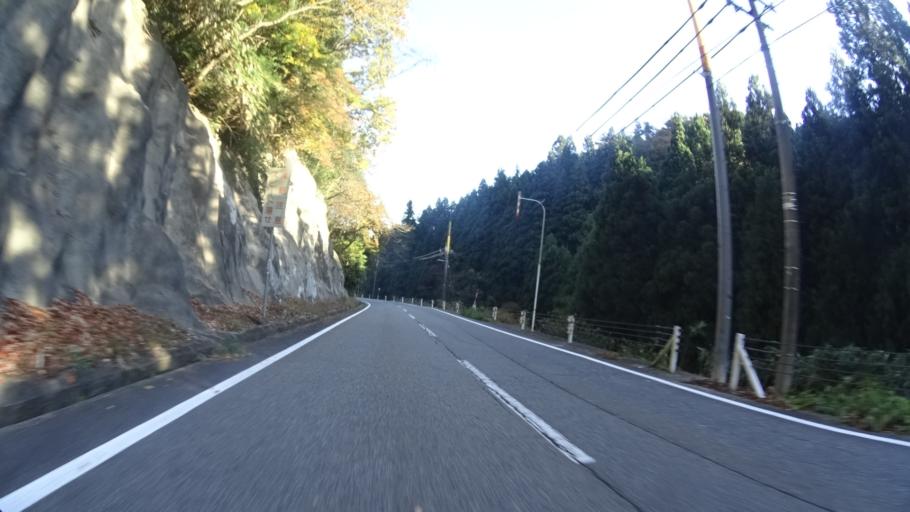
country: JP
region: Fukui
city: Maruoka
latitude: 36.1432
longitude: 136.3263
